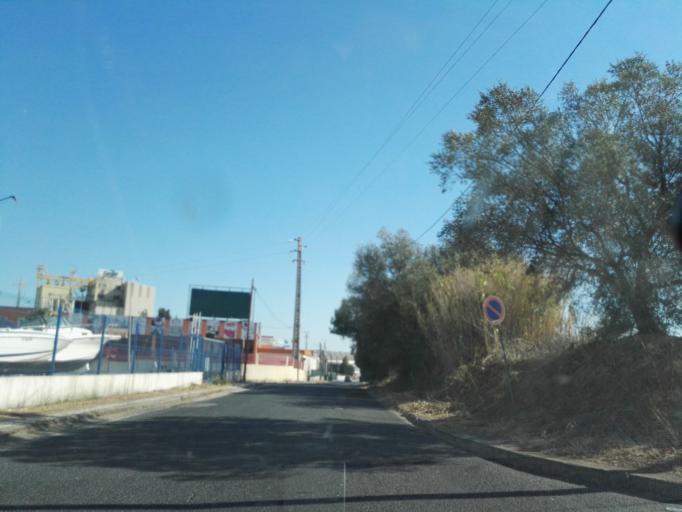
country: PT
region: Lisbon
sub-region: Vila Franca de Xira
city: Sobralinho
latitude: 38.9056
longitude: -9.0264
